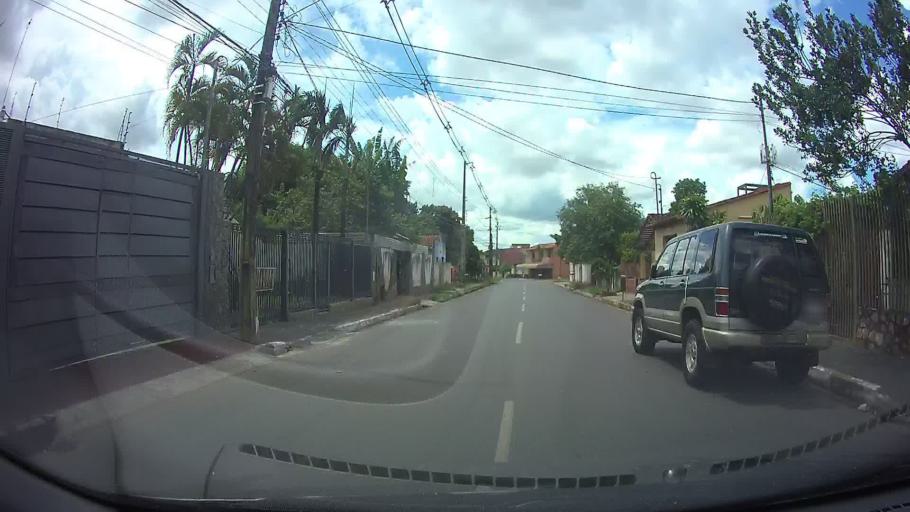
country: PY
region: Central
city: Fernando de la Mora
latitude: -25.3226
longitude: -57.5499
